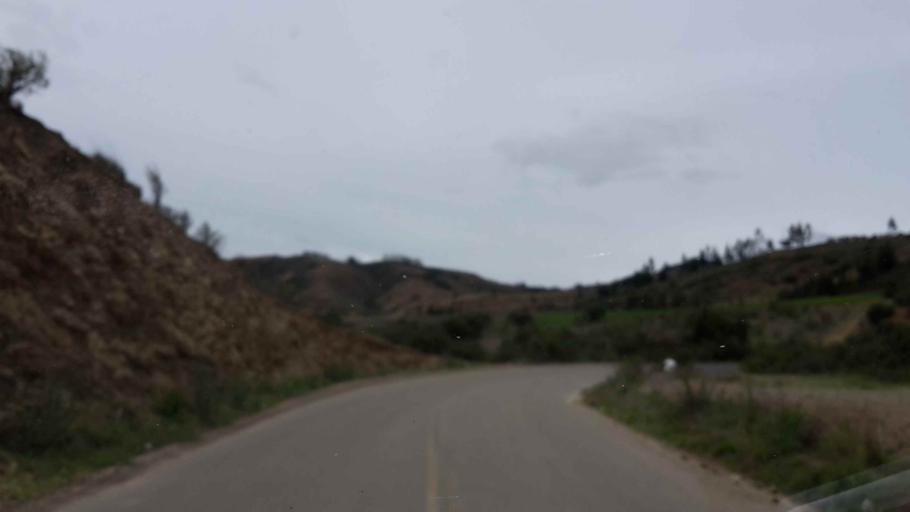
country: BO
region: Cochabamba
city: Totora
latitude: -17.7067
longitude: -65.2125
